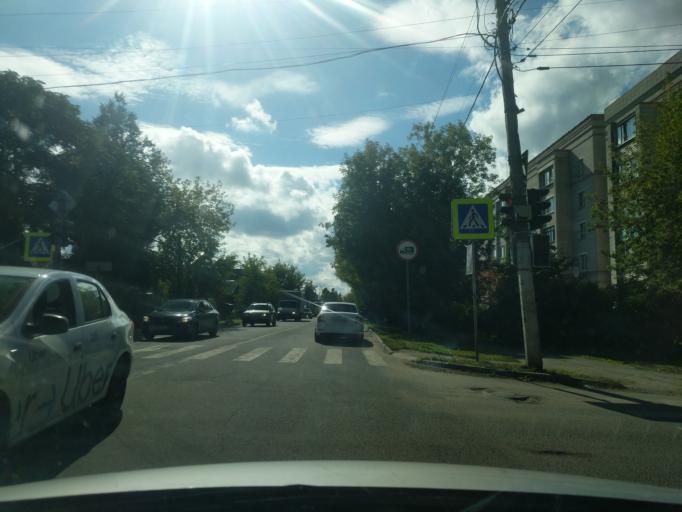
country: RU
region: Kostroma
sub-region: Kostromskoy Rayon
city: Kostroma
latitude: 57.7773
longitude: 40.9543
